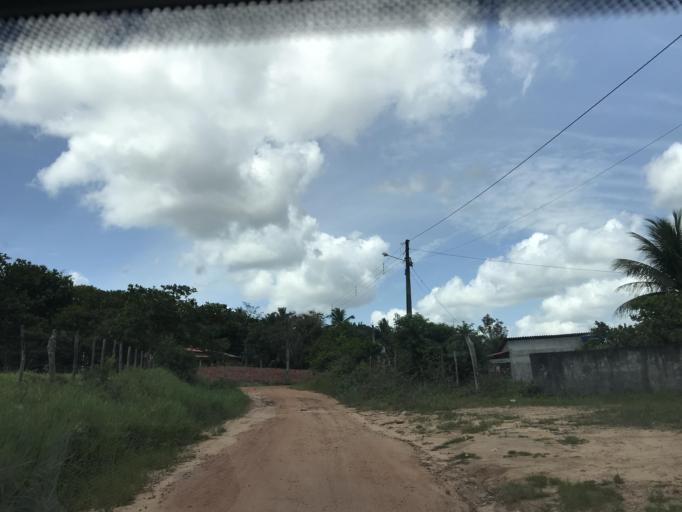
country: BR
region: Bahia
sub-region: Entre Rios
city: Entre Rios
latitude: -12.2394
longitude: -38.0980
